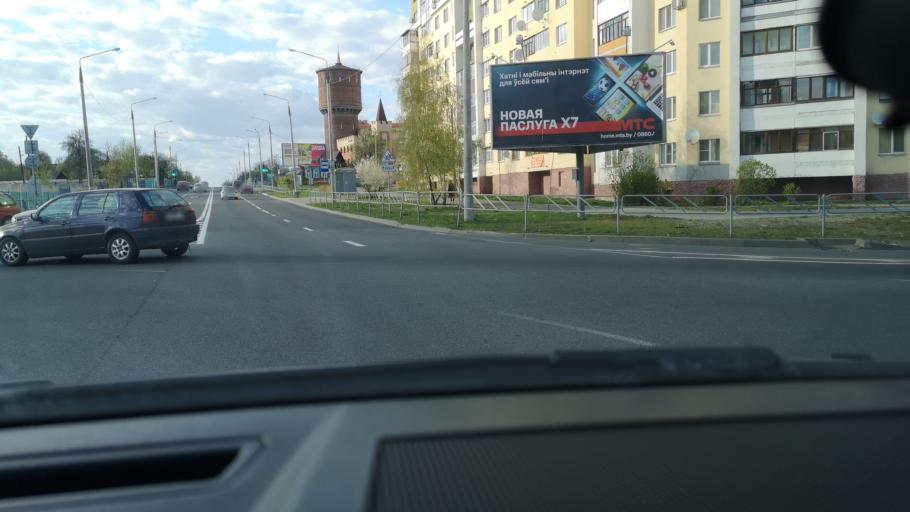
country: BY
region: Gomel
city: Gomel
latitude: 52.4398
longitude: 30.9992
